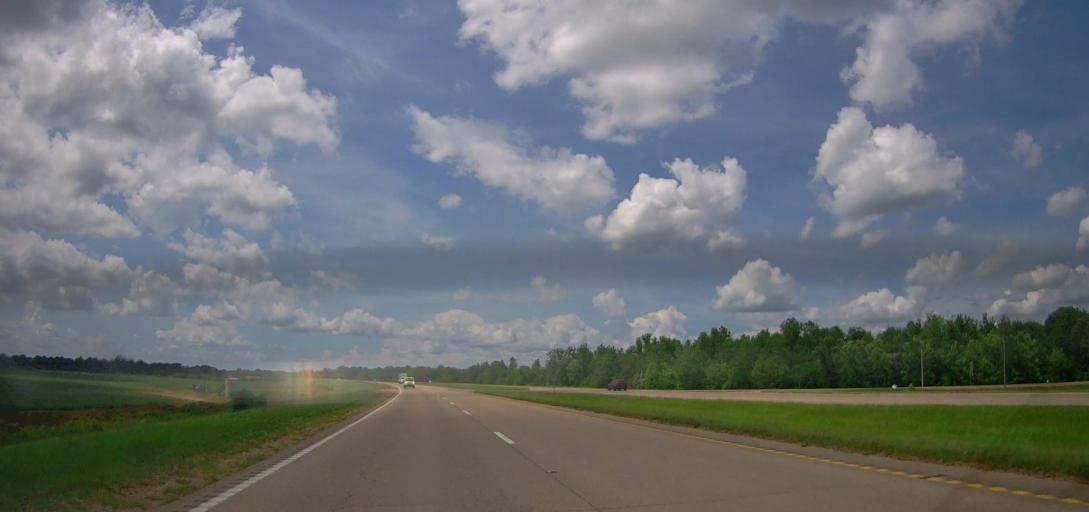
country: US
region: Mississippi
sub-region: Lee County
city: Nettleton
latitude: 34.0927
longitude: -88.6408
